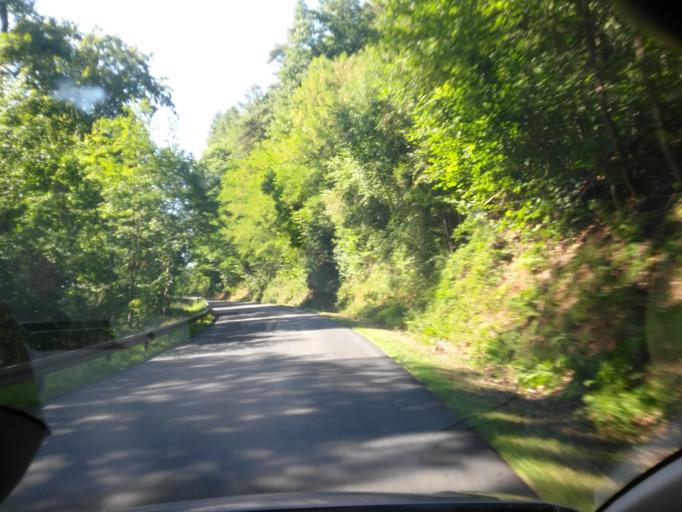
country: DE
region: Saarland
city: Orscholz
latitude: 49.4811
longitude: 6.5461
